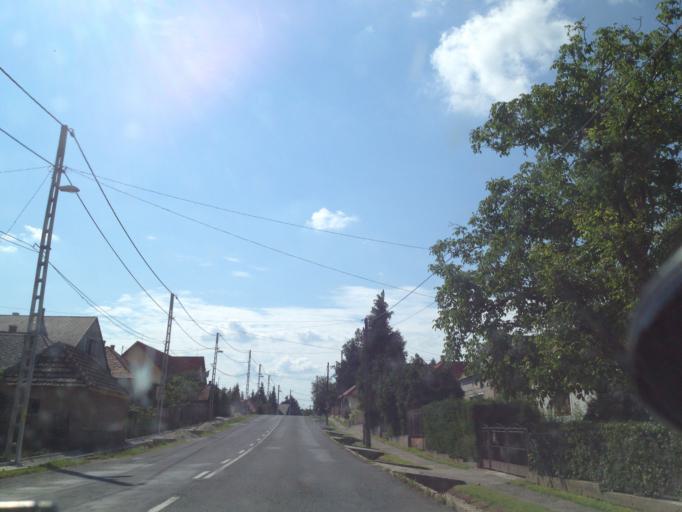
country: HU
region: Veszprem
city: Urkut
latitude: 47.2040
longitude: 17.6296
